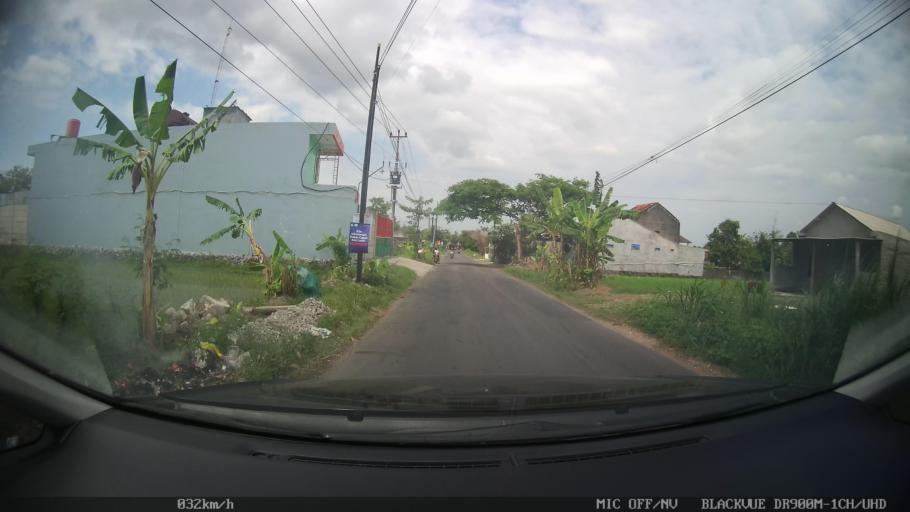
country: ID
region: Daerah Istimewa Yogyakarta
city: Depok
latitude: -7.7927
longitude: 110.4586
